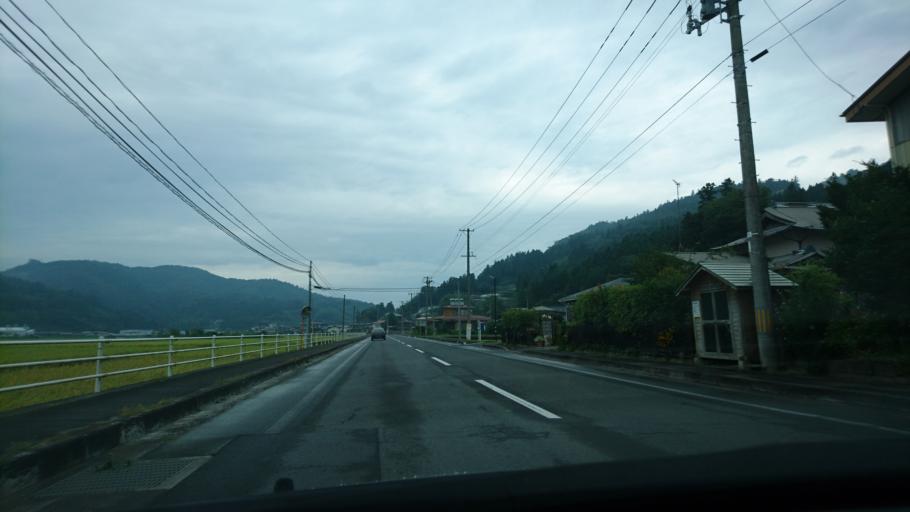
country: JP
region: Iwate
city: Ichinoseki
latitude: 38.9707
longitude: 141.2444
